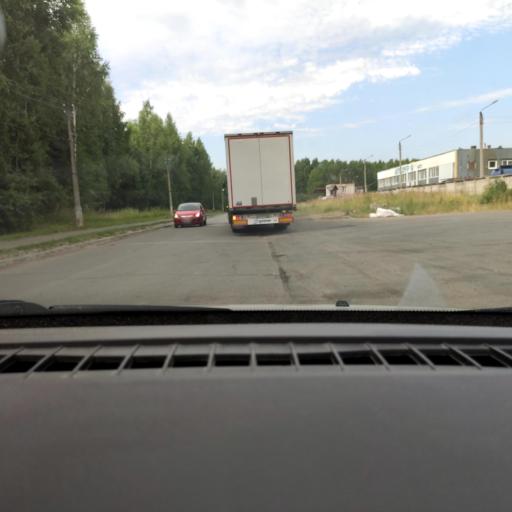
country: RU
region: Perm
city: Overyata
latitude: 58.0153
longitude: 55.9210
